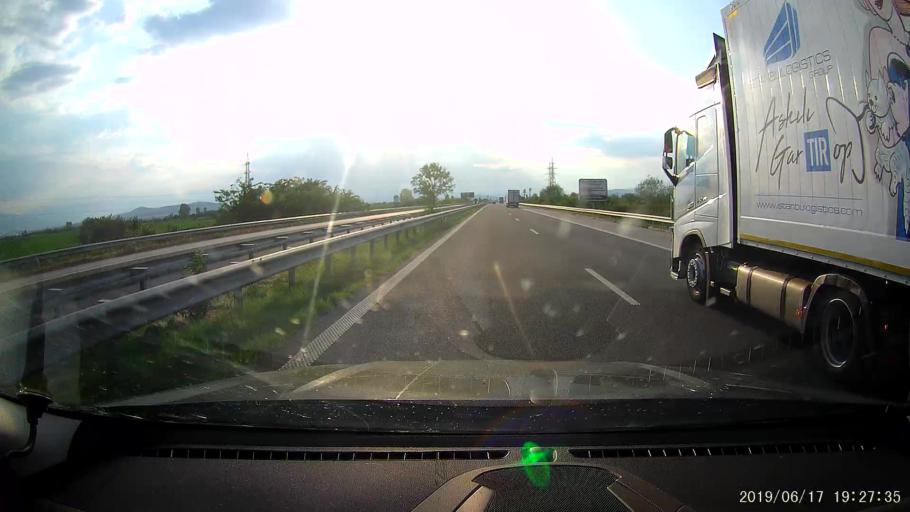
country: BG
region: Pazardzhik
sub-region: Obshtina Pazardzhik
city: Pazardzhik
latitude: 42.2676
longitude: 24.3011
